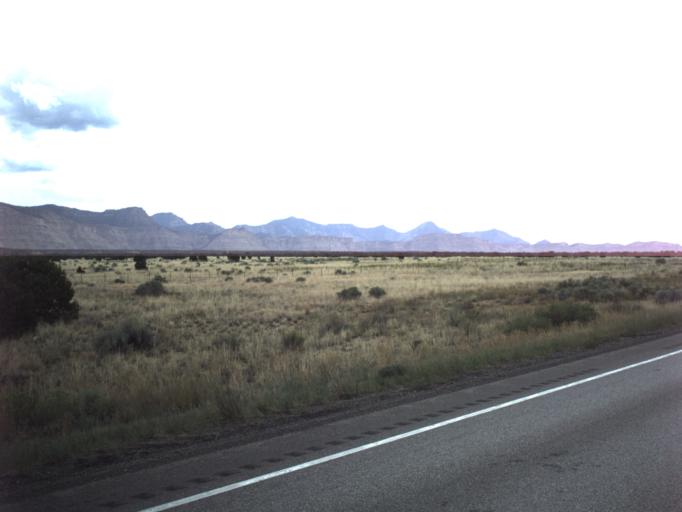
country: US
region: Utah
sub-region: Carbon County
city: East Carbon City
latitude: 39.4280
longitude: -110.4491
